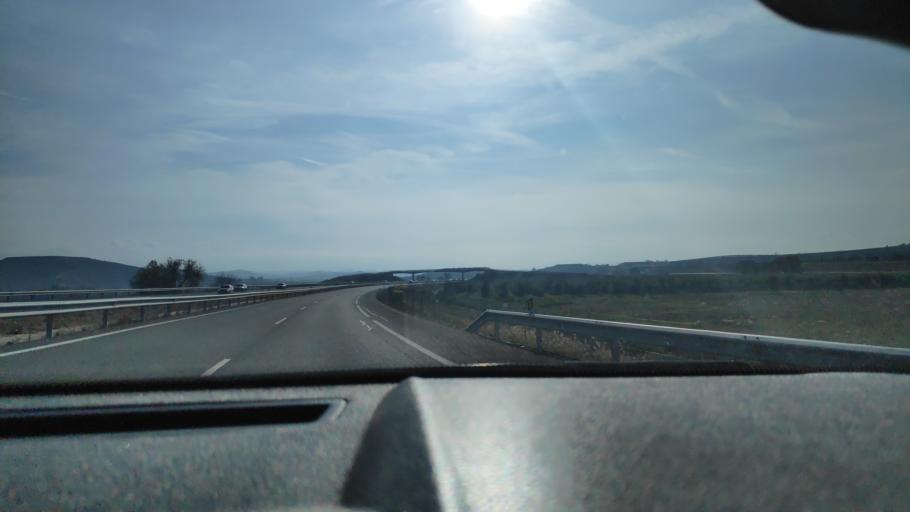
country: ES
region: Andalusia
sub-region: Provincia de Jaen
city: Mengibar
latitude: 37.8839
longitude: -3.7735
